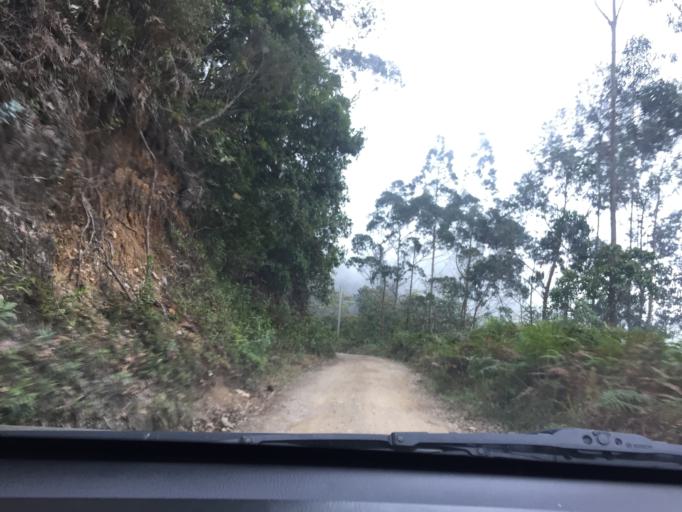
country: CO
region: Cundinamarca
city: Bojaca
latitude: 4.7061
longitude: -74.3641
